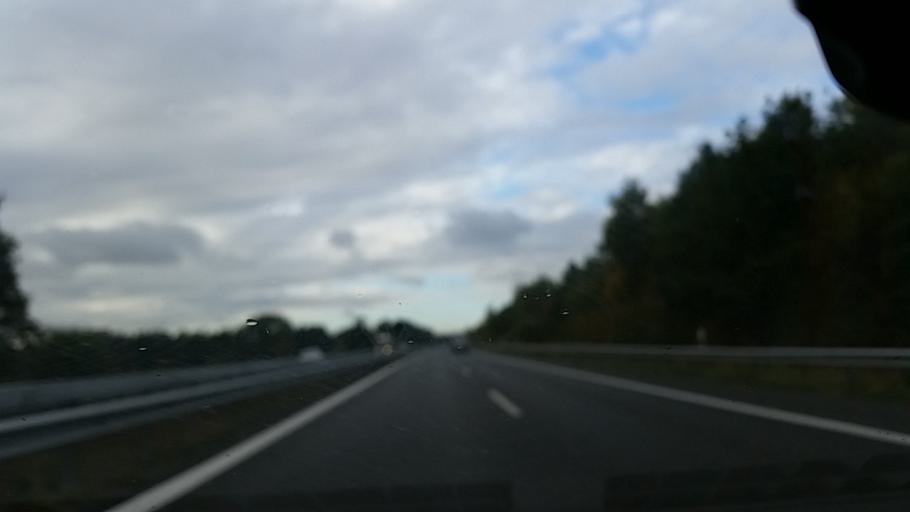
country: DE
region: Schleswig-Holstein
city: Bornsen
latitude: 53.4680
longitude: 10.2656
